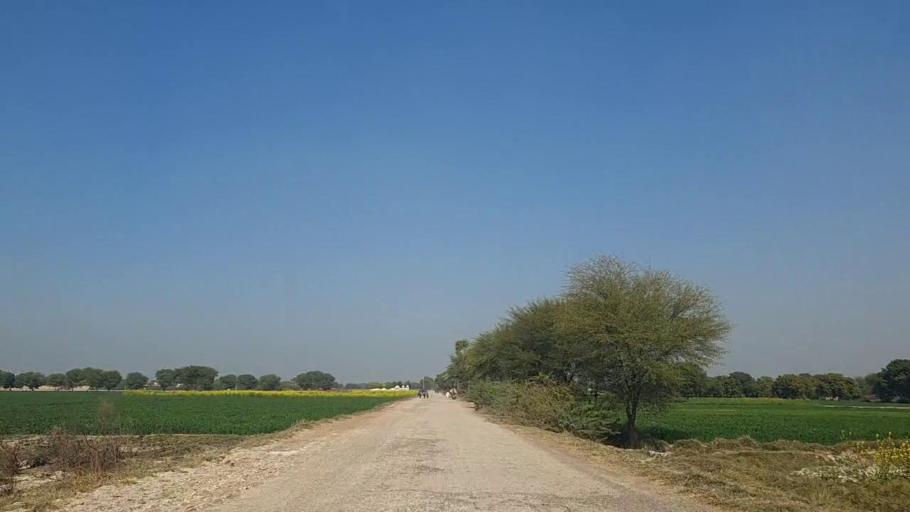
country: PK
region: Sindh
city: Nawabshah
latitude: 26.2248
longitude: 68.3379
